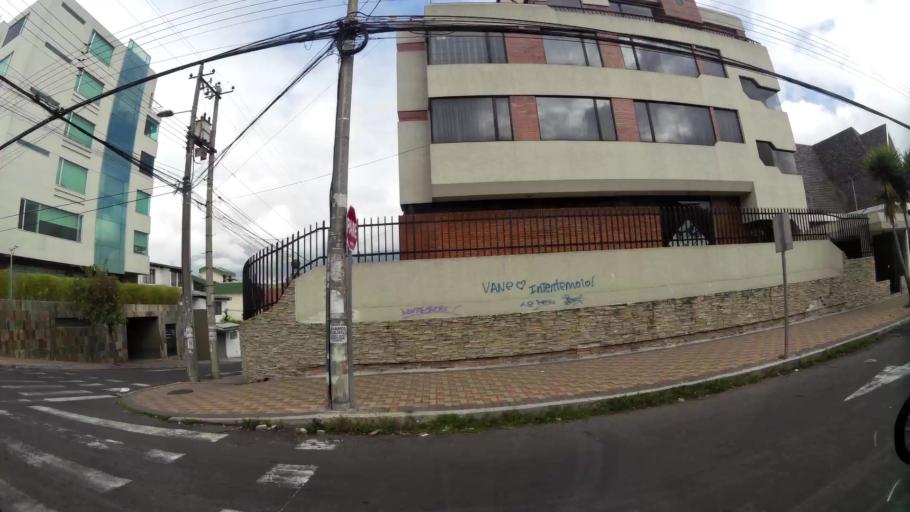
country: EC
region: Pichincha
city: Quito
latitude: -0.1739
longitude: -78.4743
